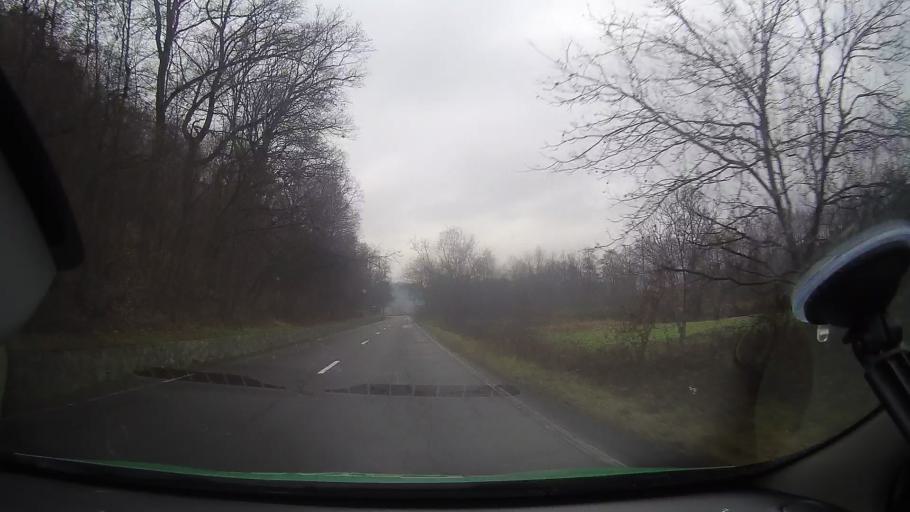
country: RO
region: Arad
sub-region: Comuna Gurahont
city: Gurahont
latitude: 46.2742
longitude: 22.3737
